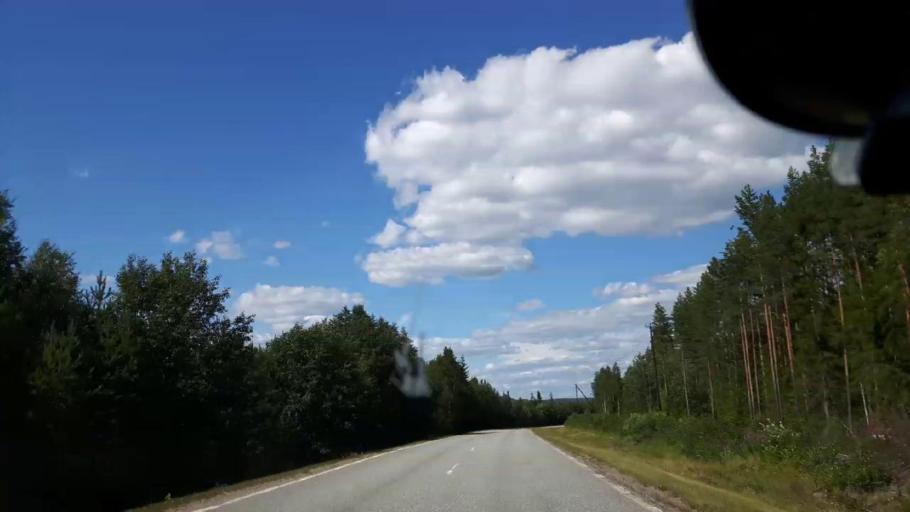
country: SE
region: Vaesternorrland
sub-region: Ange Kommun
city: Fransta
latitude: 62.7180
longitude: 16.3330
